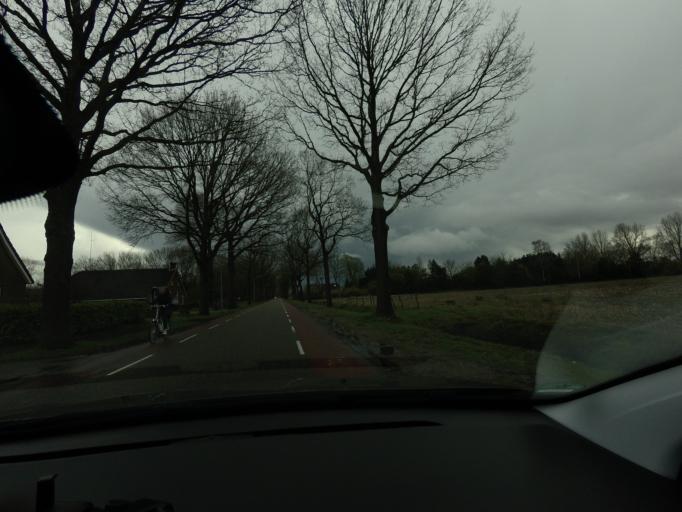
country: NL
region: Drenthe
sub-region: Gemeente Borger-Odoorn
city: Borger
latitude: 52.9824
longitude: 6.7847
